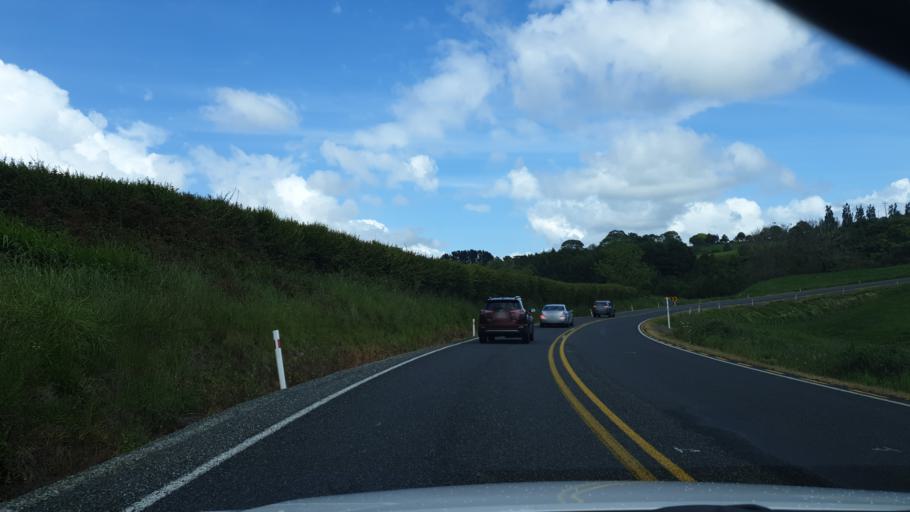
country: NZ
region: Waikato
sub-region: Matamata-Piako District
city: Matamata
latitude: -37.8810
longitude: 175.6952
